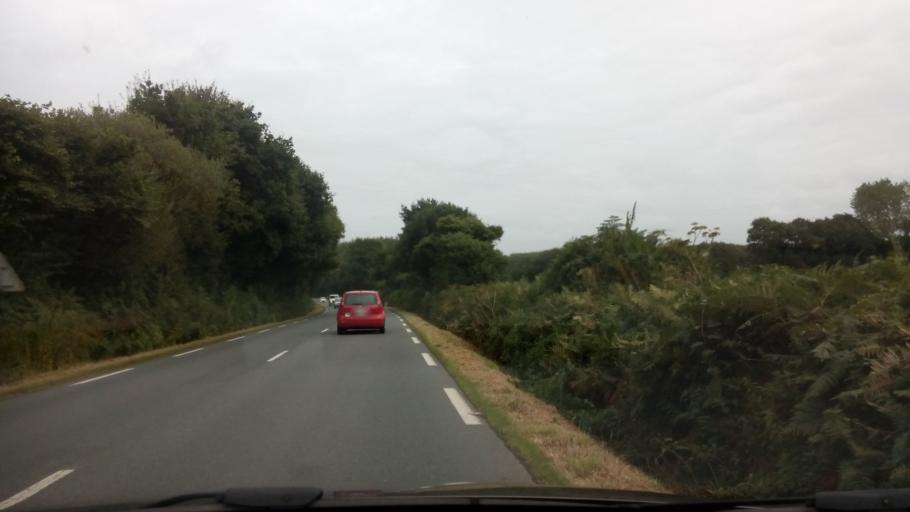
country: FR
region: Brittany
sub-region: Departement des Cotes-d'Armor
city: Ploumilliau
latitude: 48.7021
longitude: -3.5157
